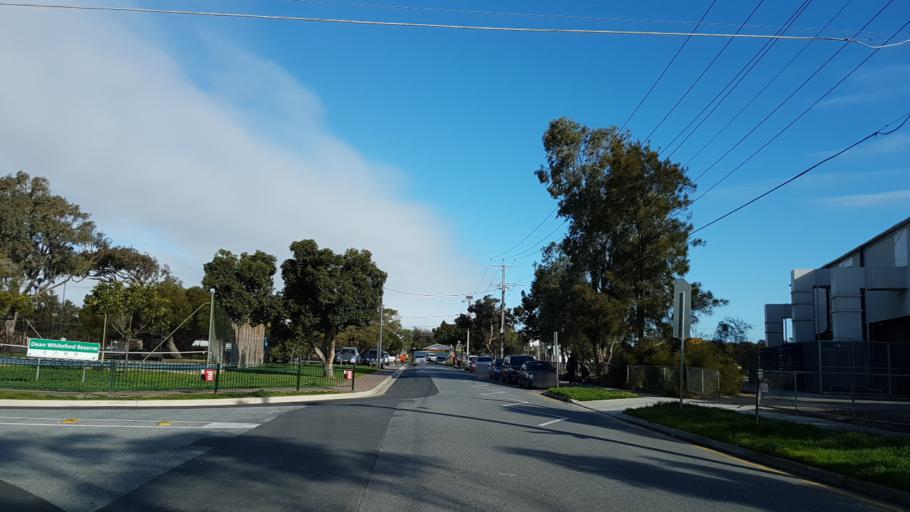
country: AU
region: South Australia
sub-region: Charles Sturt
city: Henley Beach
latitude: -34.9294
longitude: 138.5008
